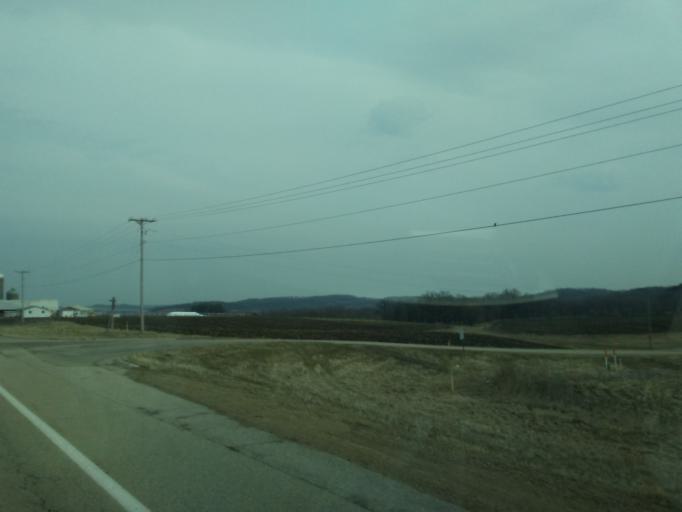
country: US
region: Wisconsin
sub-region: Columbia County
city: Lodi
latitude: 43.2646
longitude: -89.5211
